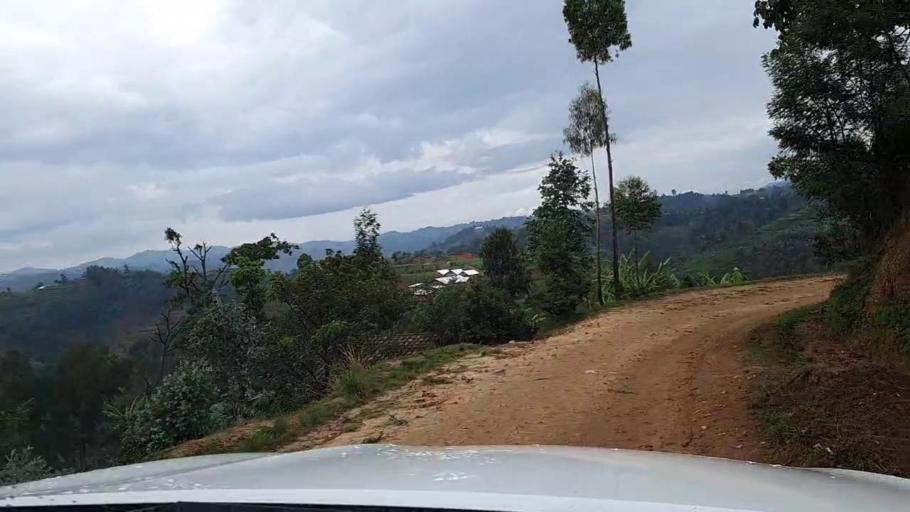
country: RW
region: Southern Province
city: Nzega
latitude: -2.4558
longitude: 29.4716
